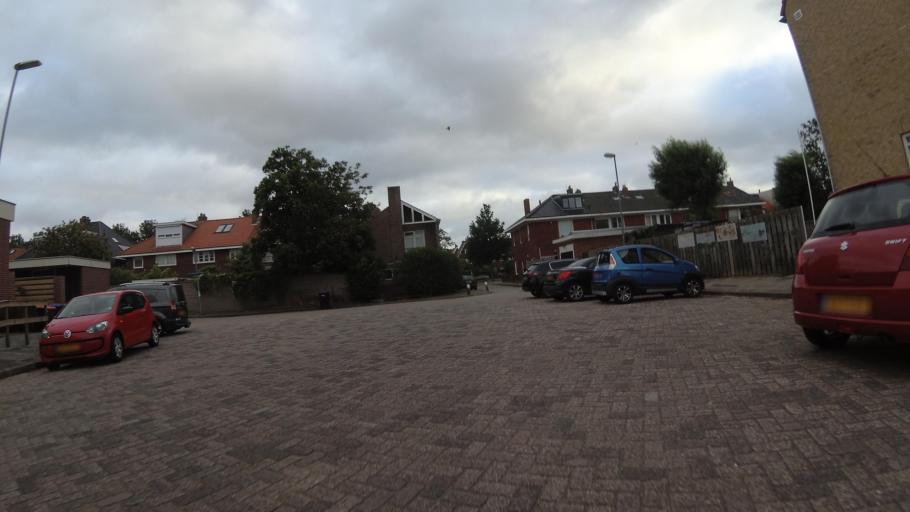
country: NL
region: North Holland
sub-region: Gemeente Den Helder
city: Den Helder
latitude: 52.9595
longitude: 4.7482
